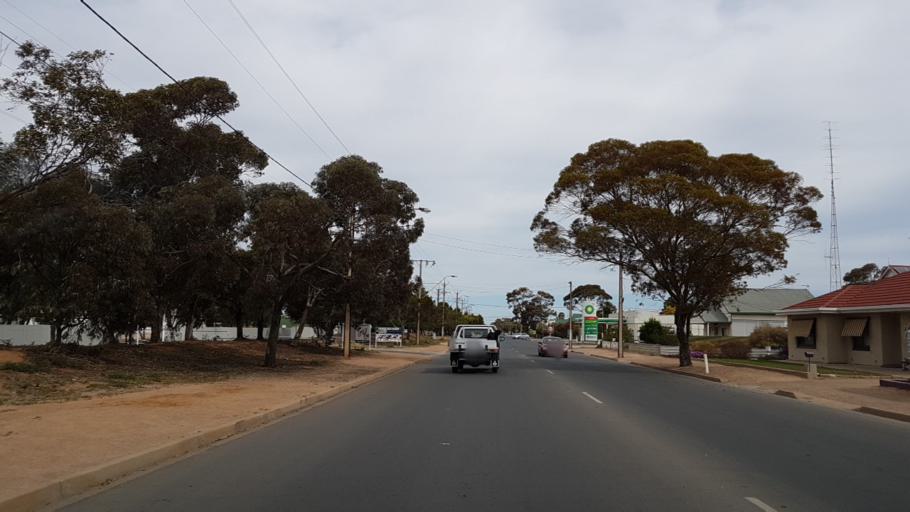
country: AU
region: South Australia
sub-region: Port Pirie City and Dists
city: Port Pirie
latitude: -33.1864
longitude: 138.0039
